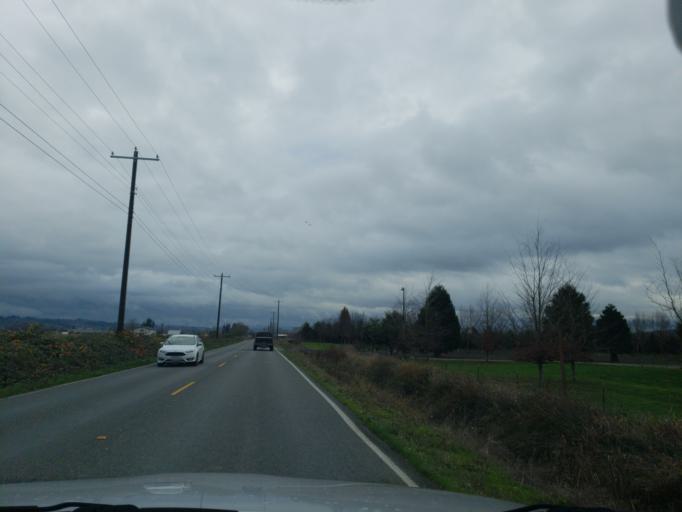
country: US
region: Washington
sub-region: Snohomish County
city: Snohomish
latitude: 47.8991
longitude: -122.1226
